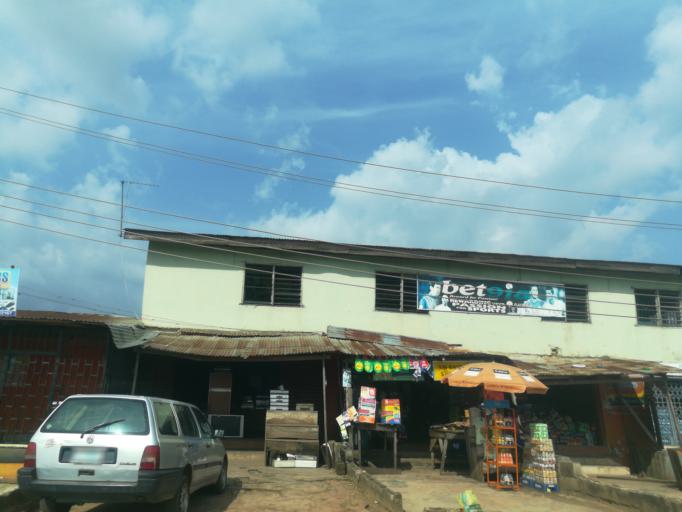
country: NG
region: Oyo
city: Ibadan
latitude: 7.3890
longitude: 3.8217
